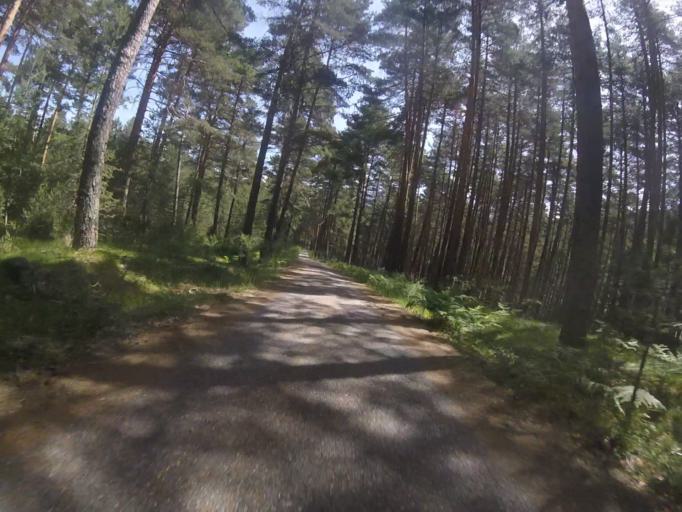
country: ES
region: Madrid
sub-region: Provincia de Madrid
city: Cercedilla
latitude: 40.8073
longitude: -4.0407
